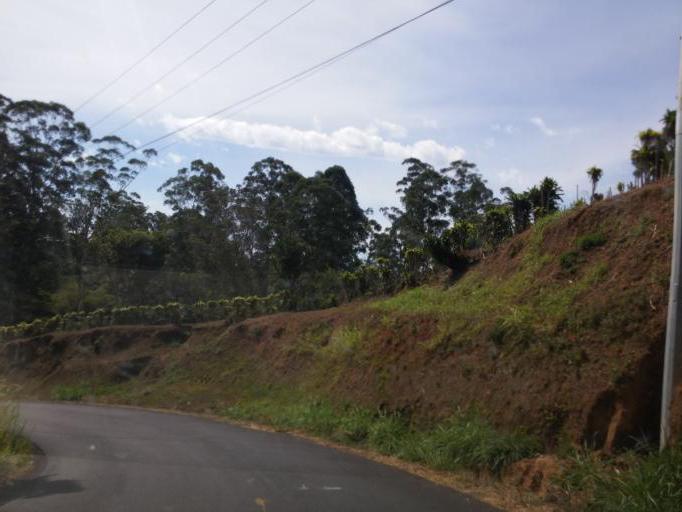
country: CR
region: Alajuela
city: Sabanilla
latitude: 10.0659
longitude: -84.2078
